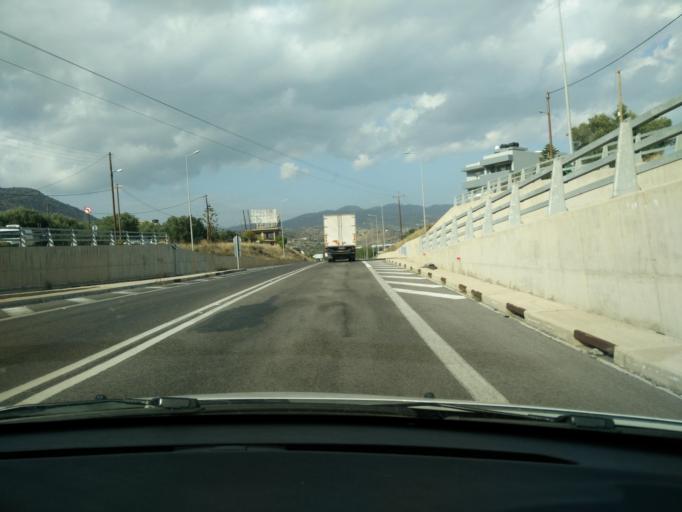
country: GR
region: Crete
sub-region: Nomos Lasithiou
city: Agios Nikolaos
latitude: 35.1865
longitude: 25.7044
